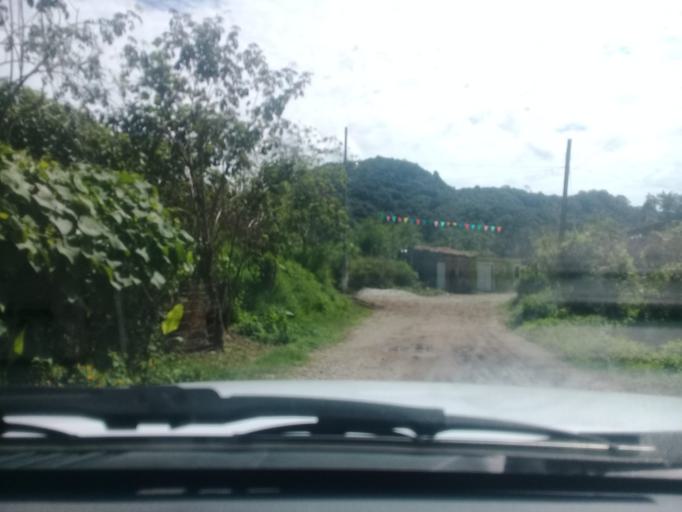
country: MX
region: Veracruz
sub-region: Tlalnelhuayocan
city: Otilpan
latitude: 19.5663
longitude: -96.9819
